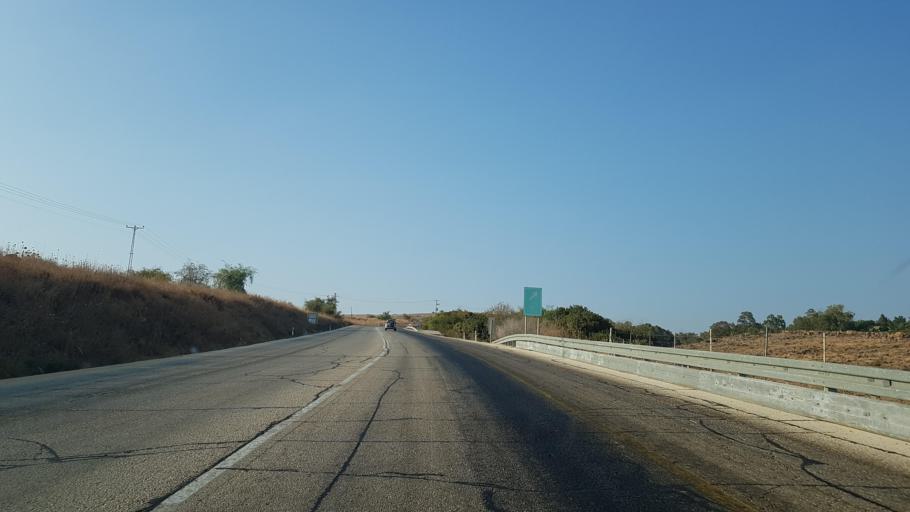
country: SY
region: Quneitra
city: Al Butayhah
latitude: 32.9043
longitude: 35.5978
